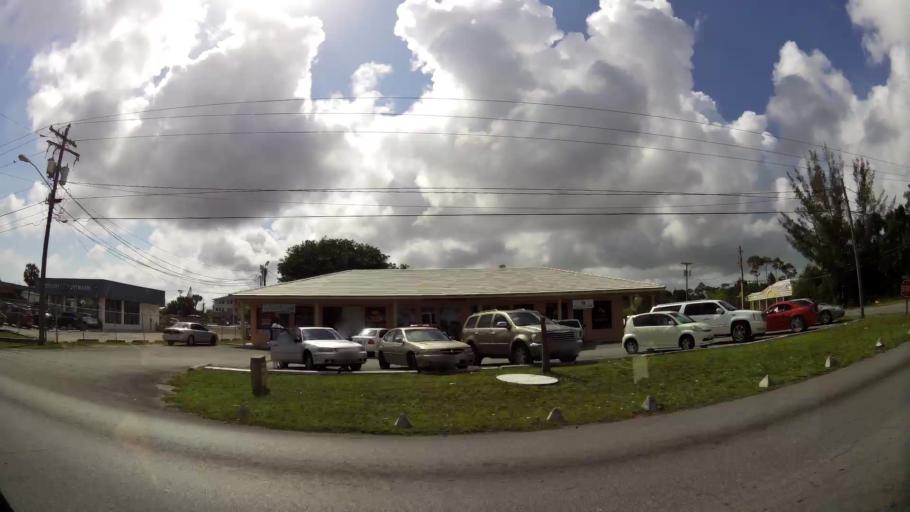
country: BS
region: Freeport
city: Freeport
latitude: 26.5339
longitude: -78.6972
